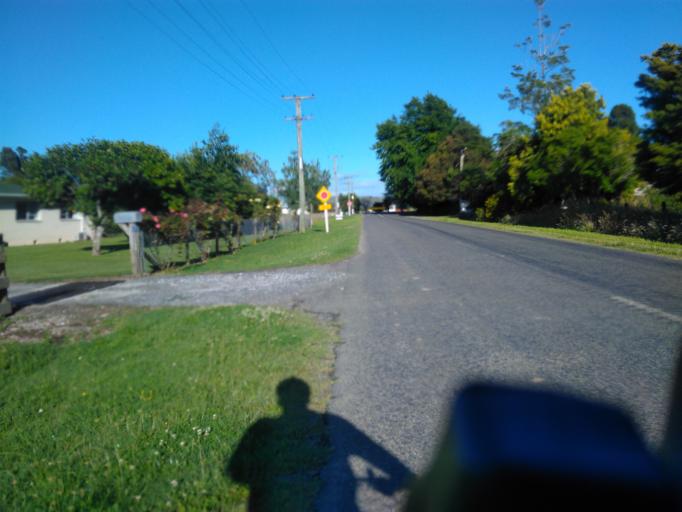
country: NZ
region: Gisborne
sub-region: Gisborne District
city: Gisborne
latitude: -38.5979
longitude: 177.9269
